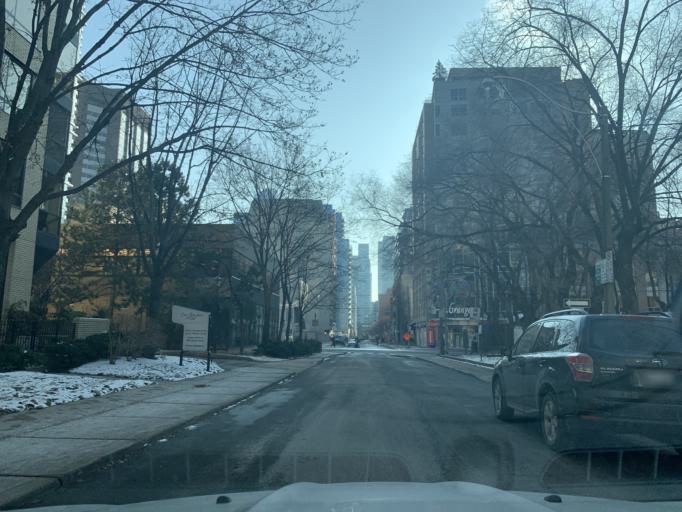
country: CA
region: Ontario
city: Toronto
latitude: 43.6551
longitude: -79.3906
